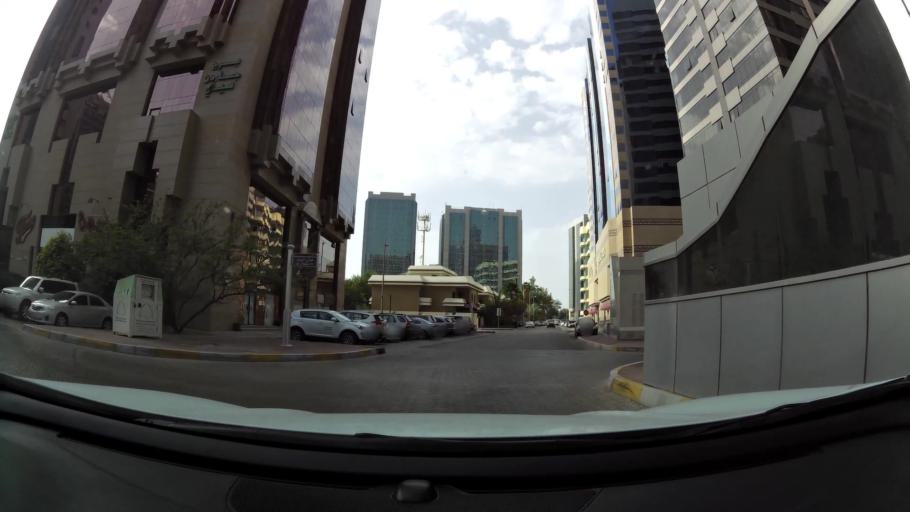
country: AE
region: Abu Dhabi
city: Abu Dhabi
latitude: 24.4735
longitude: 54.3472
